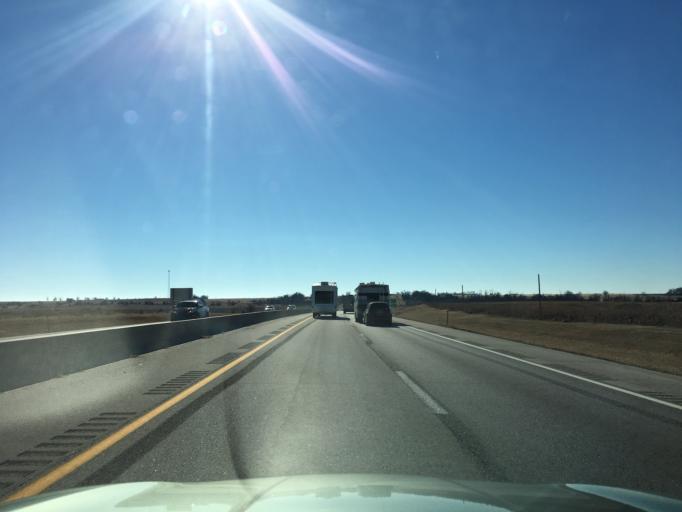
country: US
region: Oklahoma
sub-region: Kay County
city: Blackwell
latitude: 37.0132
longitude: -97.3386
